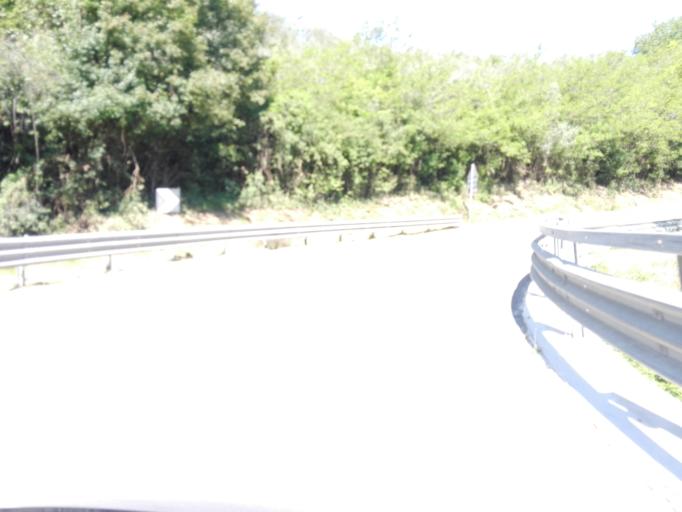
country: IT
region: Umbria
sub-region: Provincia di Perugia
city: Foligno
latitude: 42.9618
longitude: 12.7440
